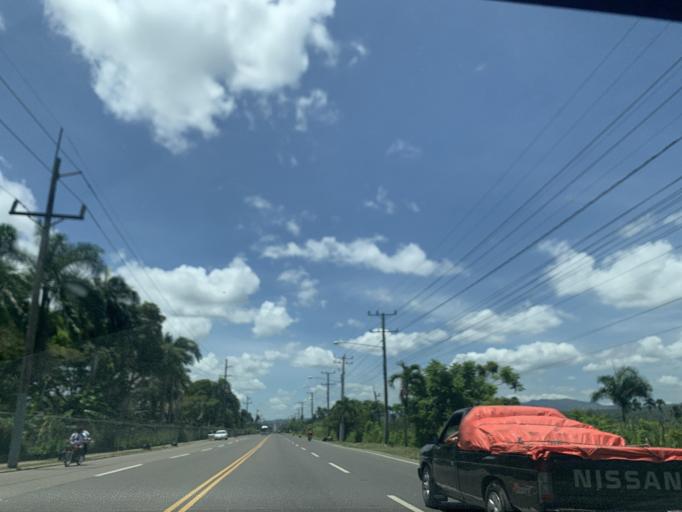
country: DO
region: Puerto Plata
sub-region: Puerto Plata
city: Puerto Plata
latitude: 19.7622
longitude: -70.6479
